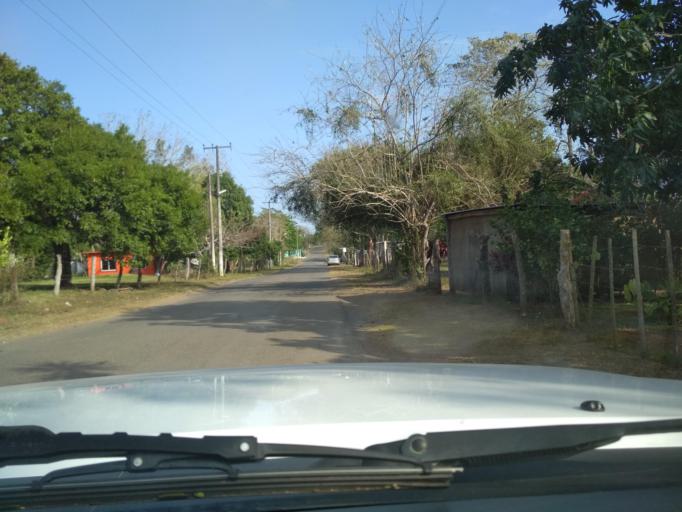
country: MX
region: Veracruz
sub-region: Veracruz
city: Delfino Victoria (Santa Fe)
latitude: 19.1536
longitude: -96.3024
